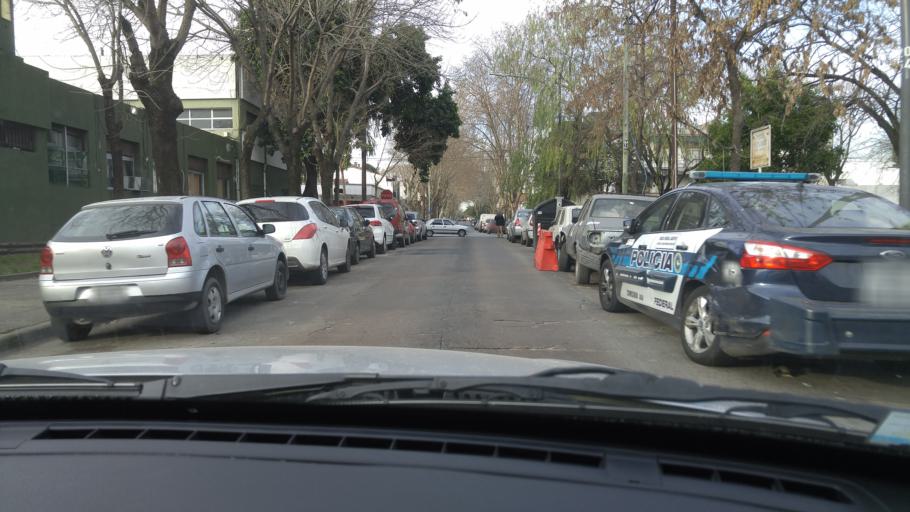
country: AR
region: Buenos Aires F.D.
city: Villa Santa Rita
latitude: -34.6300
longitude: -58.5243
